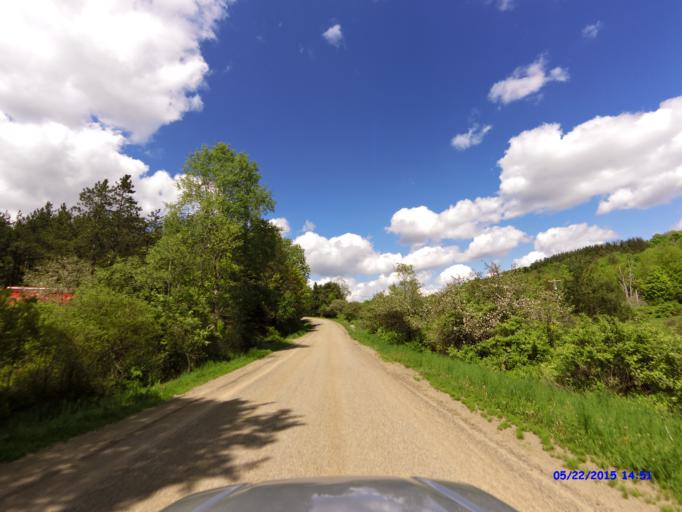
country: US
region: New York
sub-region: Cattaraugus County
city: Franklinville
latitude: 42.3772
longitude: -78.5746
